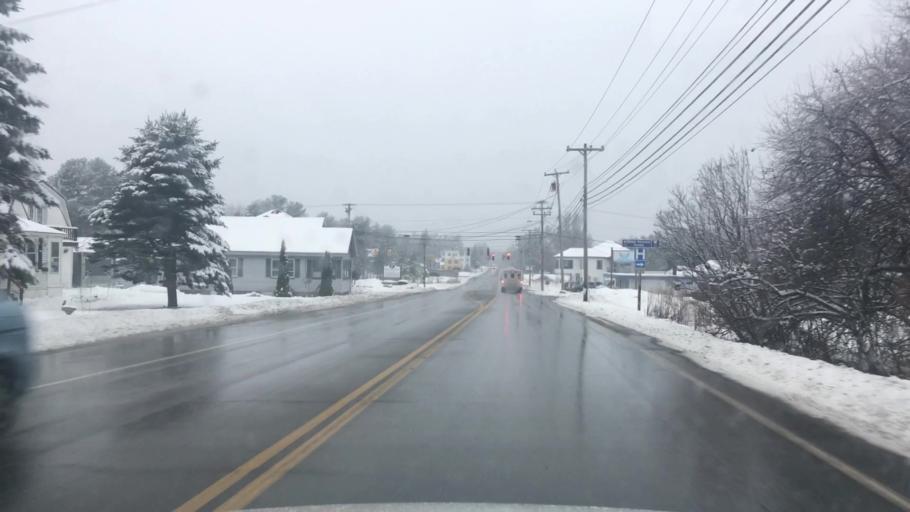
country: US
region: Maine
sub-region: Kennebec County
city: Augusta
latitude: 44.3034
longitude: -69.7411
